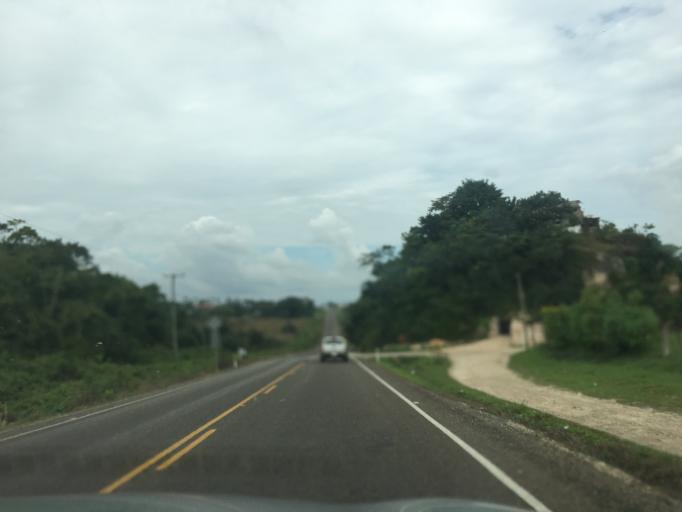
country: BZ
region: Cayo
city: Belmopan
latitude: 17.2311
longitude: -88.7796
